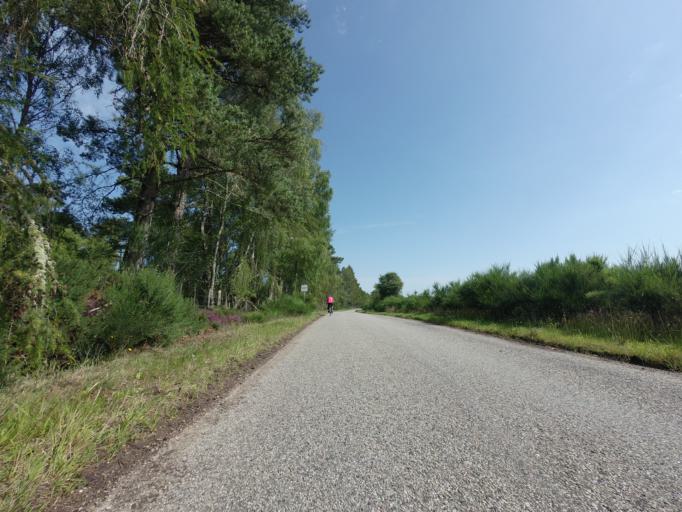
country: GB
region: Scotland
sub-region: Highland
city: Invergordon
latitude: 57.7348
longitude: -4.1903
